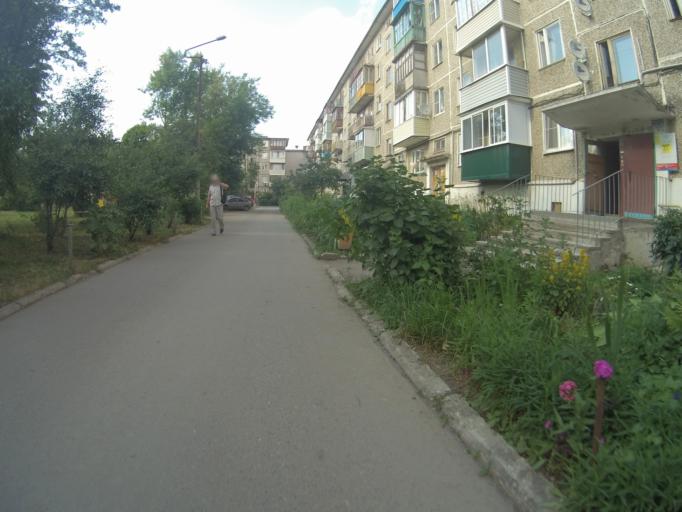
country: RU
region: Vladimir
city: Bogolyubovo
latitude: 56.1736
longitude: 40.4870
